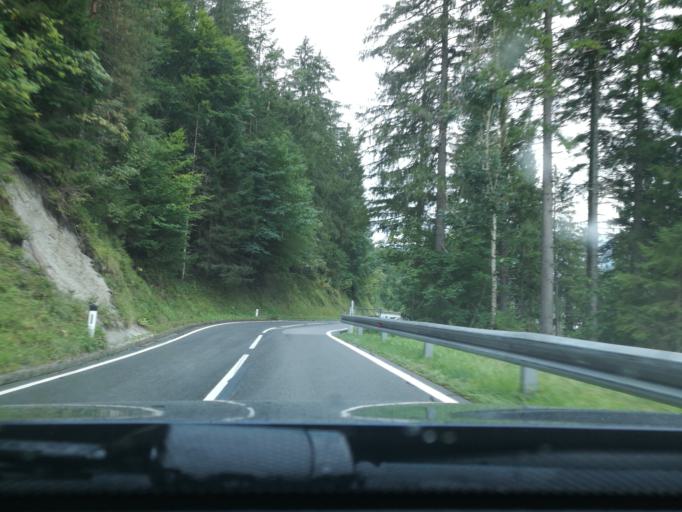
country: AT
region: Salzburg
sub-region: Politischer Bezirk Sankt Johann im Pongau
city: Radstadt
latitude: 47.3814
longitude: 13.4863
